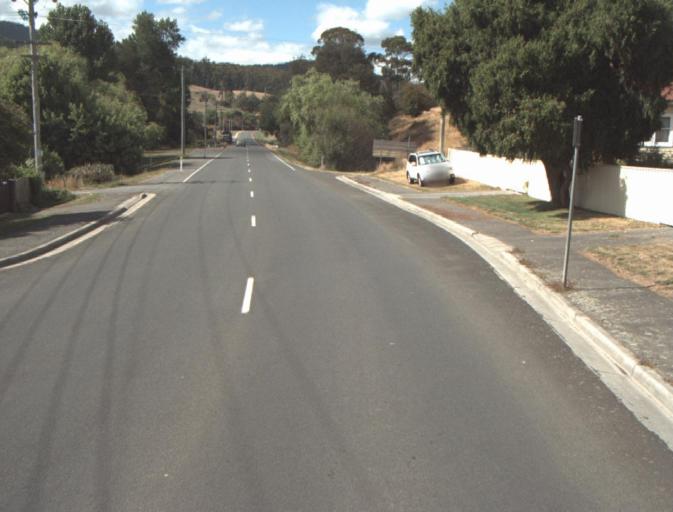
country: AU
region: Tasmania
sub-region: Launceston
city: Mayfield
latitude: -41.2543
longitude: 147.2157
